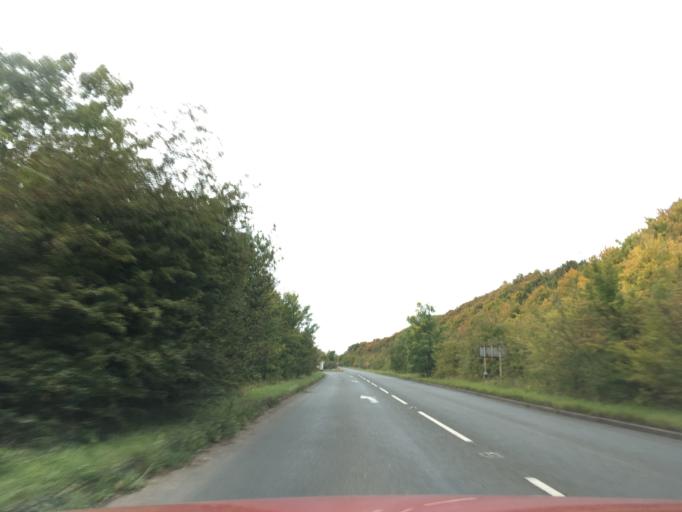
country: GB
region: England
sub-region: South Gloucestershire
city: Almondsbury
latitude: 51.5979
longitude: -2.6099
